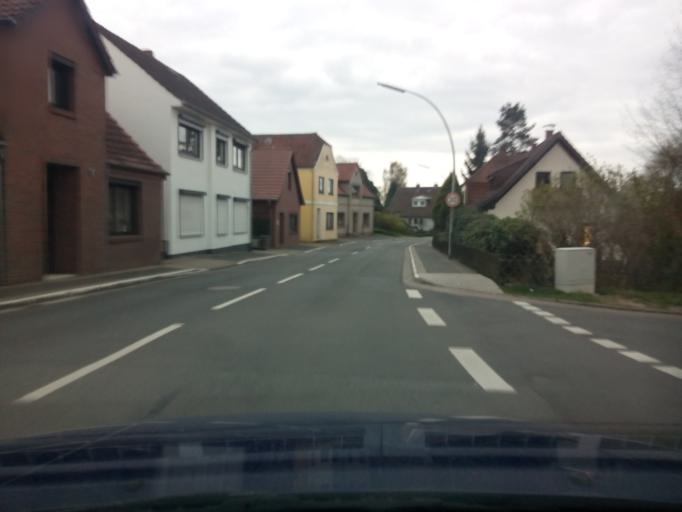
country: DE
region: Lower Saxony
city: Osterholz-Scharmbeck
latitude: 53.2357
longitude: 8.7851
